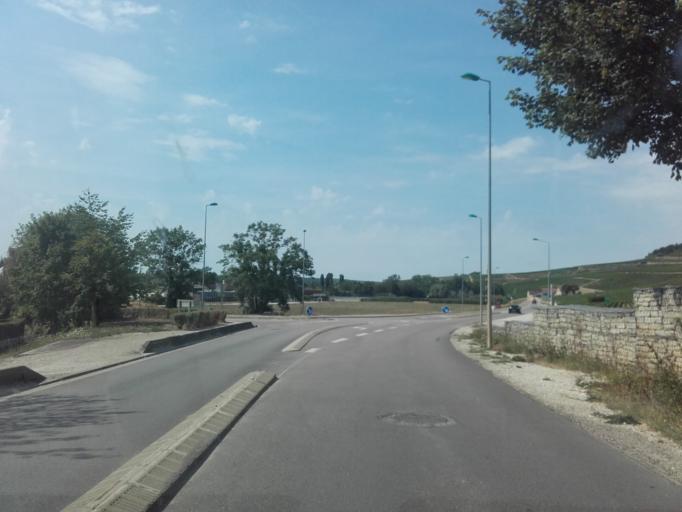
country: FR
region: Bourgogne
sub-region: Departement de l'Yonne
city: Chablis
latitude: 47.8165
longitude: 3.8081
